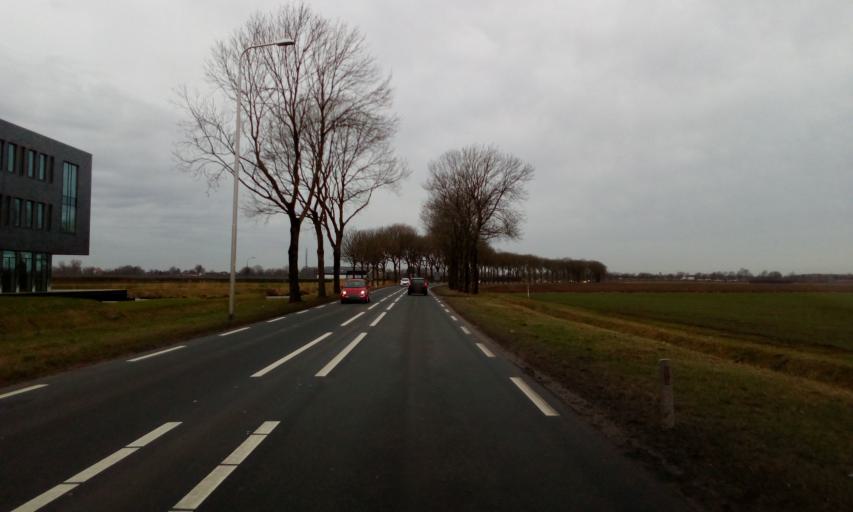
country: NL
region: North Brabant
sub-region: Gemeente Woudrichem
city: Almkerk
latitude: 51.7713
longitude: 4.9401
